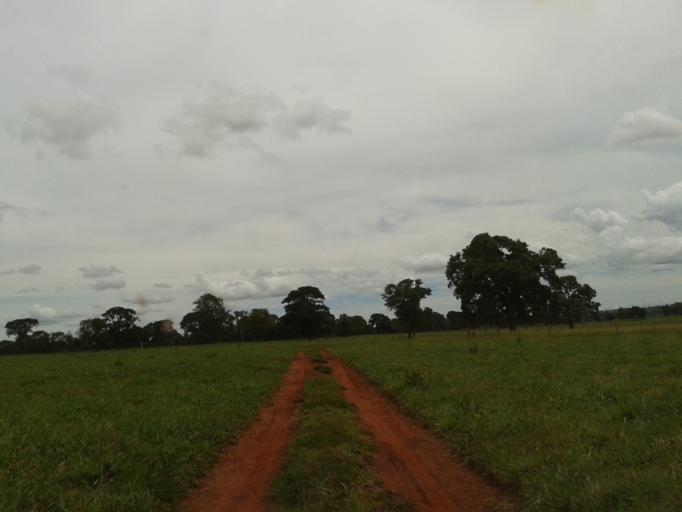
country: BR
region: Minas Gerais
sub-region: Santa Vitoria
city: Santa Vitoria
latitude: -18.7862
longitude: -49.8518
